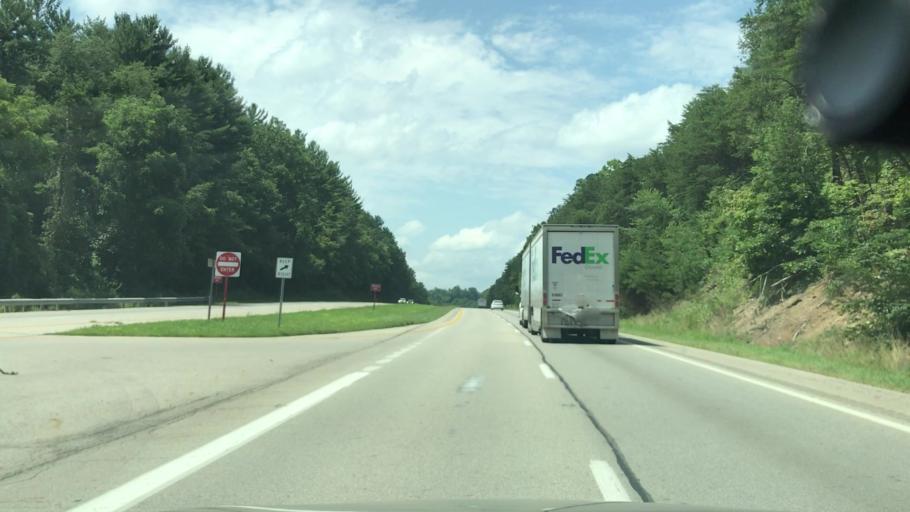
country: US
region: Ohio
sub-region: Jackson County
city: Jackson
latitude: 39.1158
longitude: -82.6827
